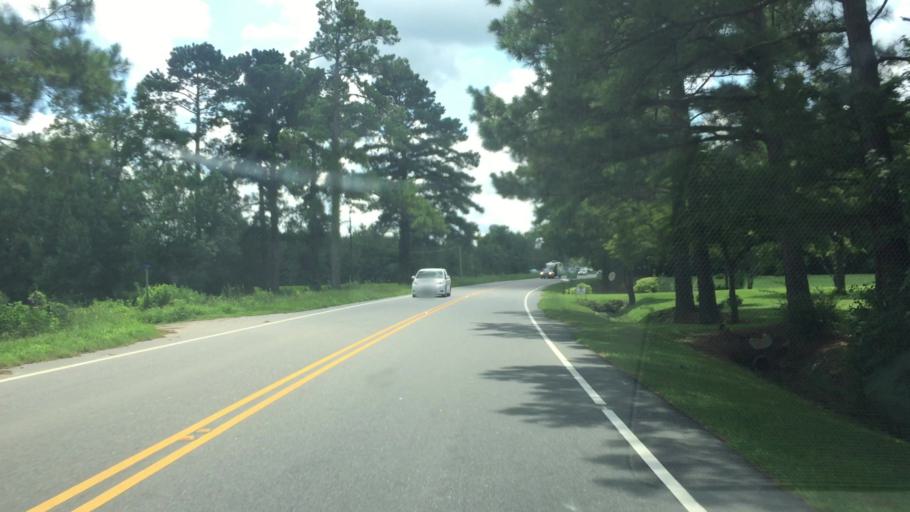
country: US
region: North Carolina
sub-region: Columbus County
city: Chadbourn
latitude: 34.2730
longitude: -78.8128
